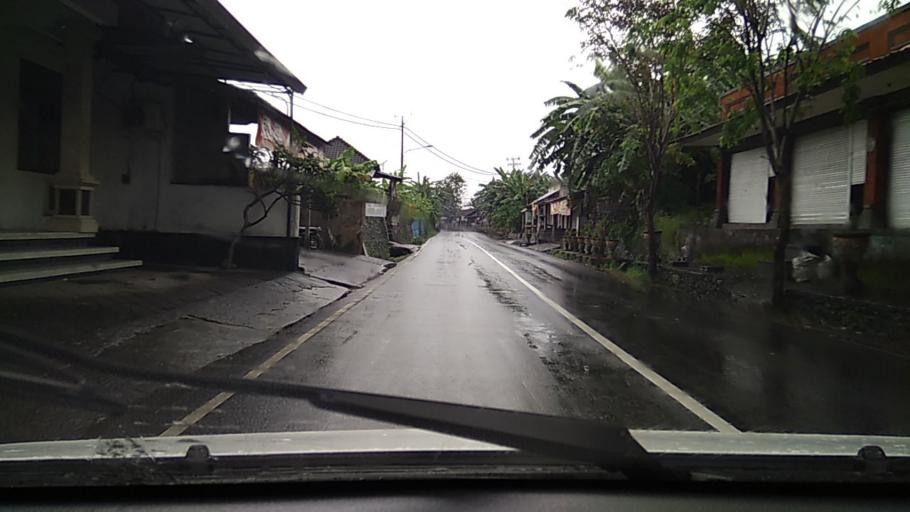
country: ID
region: Bali
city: Banjar Bugbug
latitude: -8.4916
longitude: 115.5925
